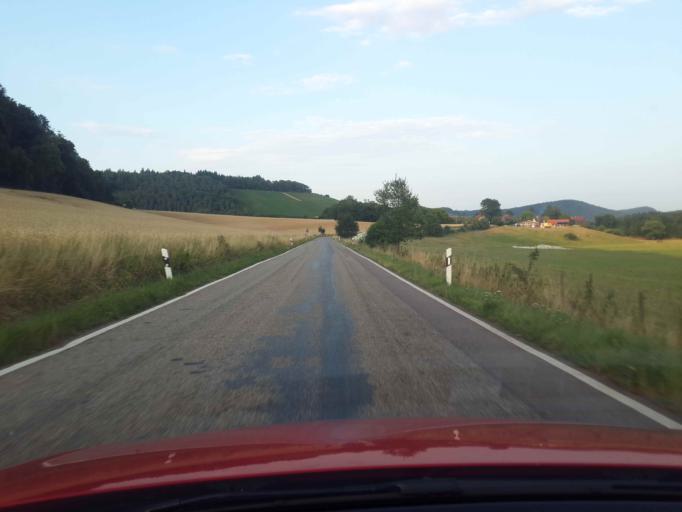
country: DE
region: Baden-Wuerttemberg
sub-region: Regierungsbezirk Stuttgart
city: Zaberfeld
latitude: 49.0184
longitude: 8.9531
